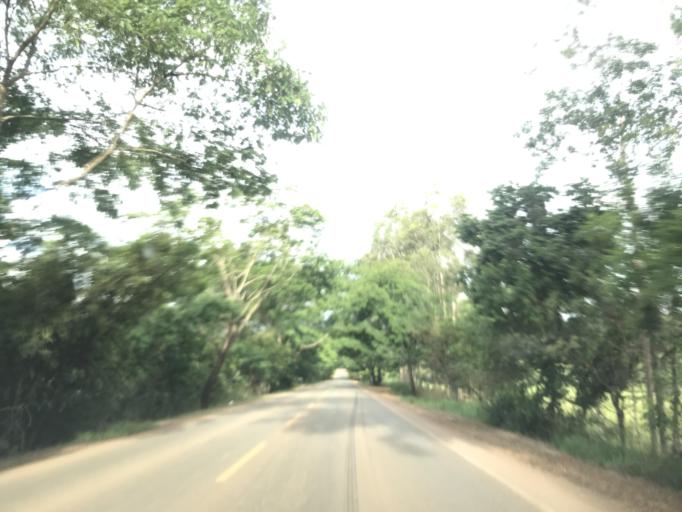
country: BR
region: Goias
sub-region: Vianopolis
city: Vianopolis
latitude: -16.5778
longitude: -48.3351
